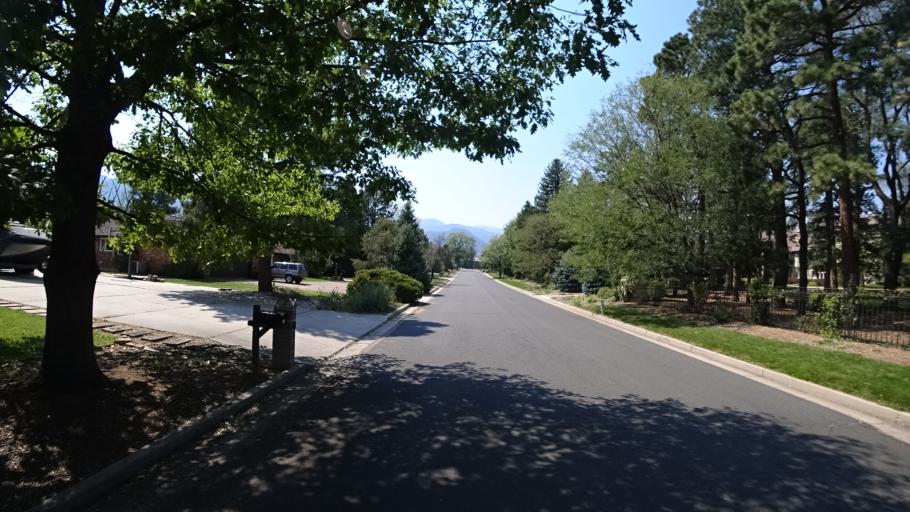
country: US
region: Colorado
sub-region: El Paso County
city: Colorado Springs
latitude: 38.7970
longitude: -104.8419
